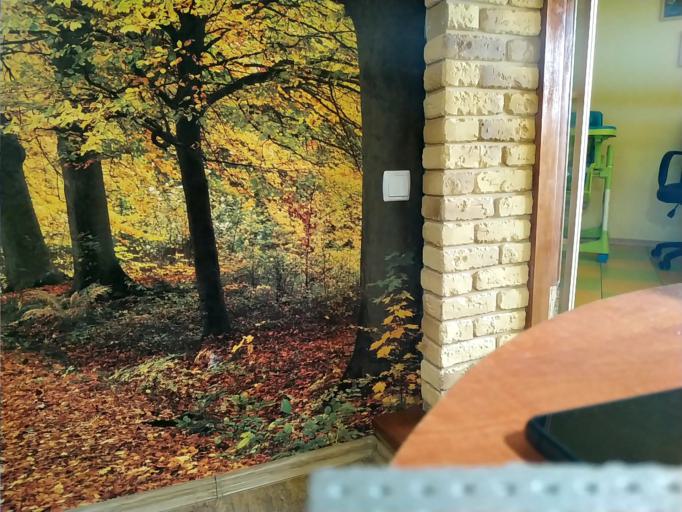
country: RU
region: Jaroslavl
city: Levashevo
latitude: 57.6562
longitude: 40.6384
